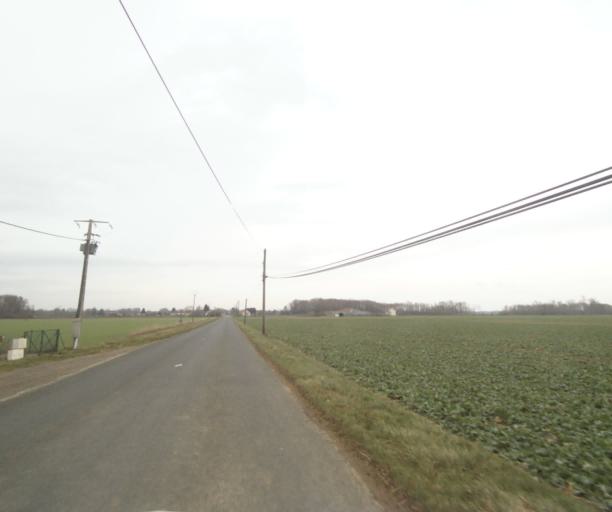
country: FR
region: Champagne-Ardenne
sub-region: Departement de la Haute-Marne
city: Villiers-en-Lieu
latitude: 48.6367
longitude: 4.8645
